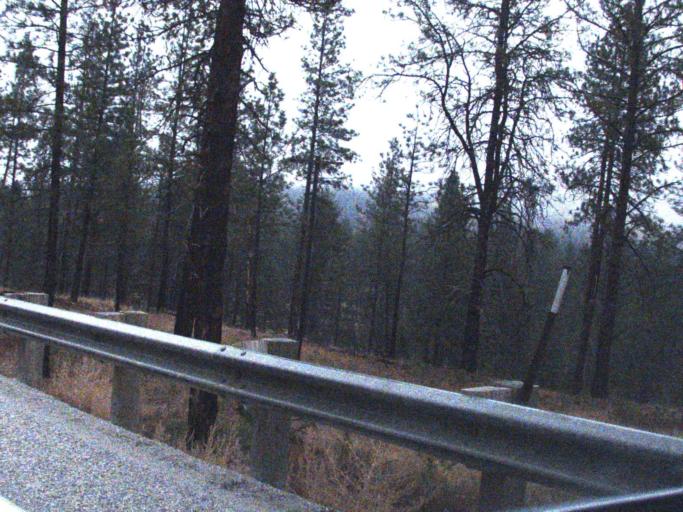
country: US
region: Washington
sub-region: Stevens County
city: Kettle Falls
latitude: 48.7547
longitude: -118.1345
